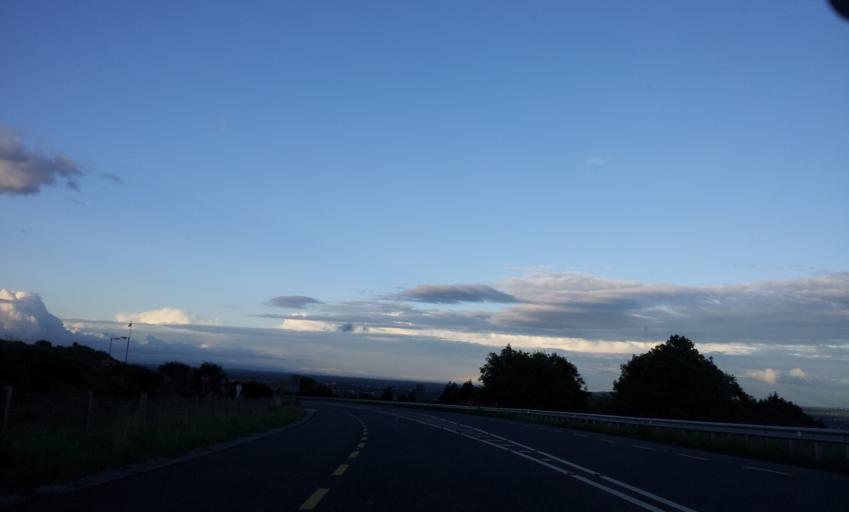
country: IE
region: Munster
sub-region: County Limerick
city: Newcastle West
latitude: 52.4211
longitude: -9.1325
